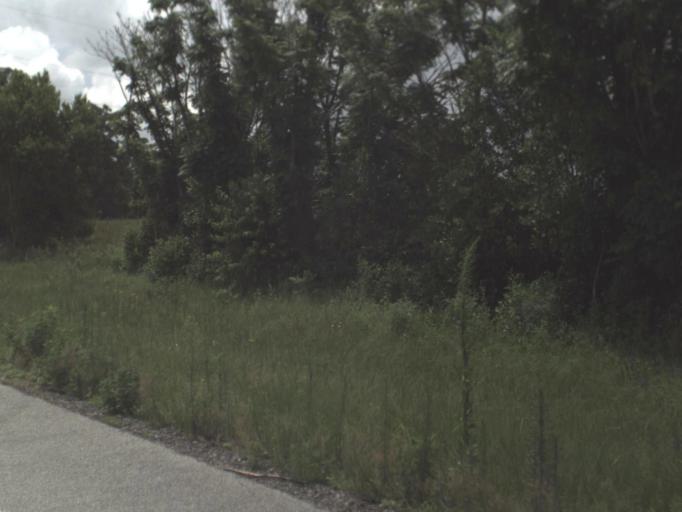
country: US
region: Florida
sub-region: Madison County
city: Madison
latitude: 30.4722
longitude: -83.2820
